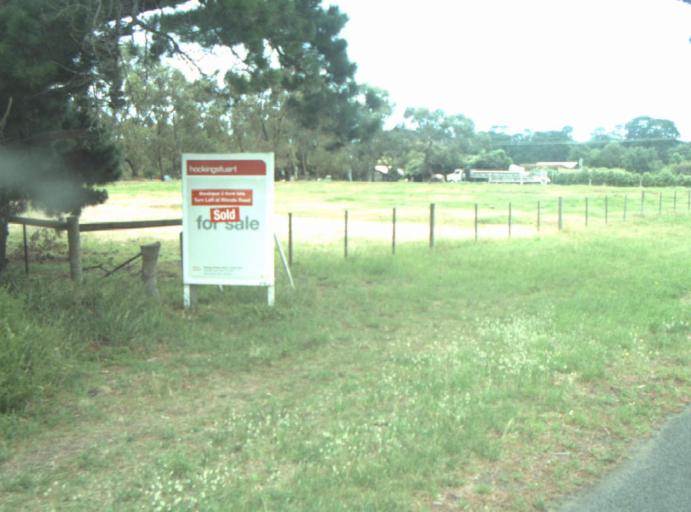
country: AU
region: Victoria
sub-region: Greater Geelong
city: Leopold
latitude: -38.2230
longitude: 144.5049
